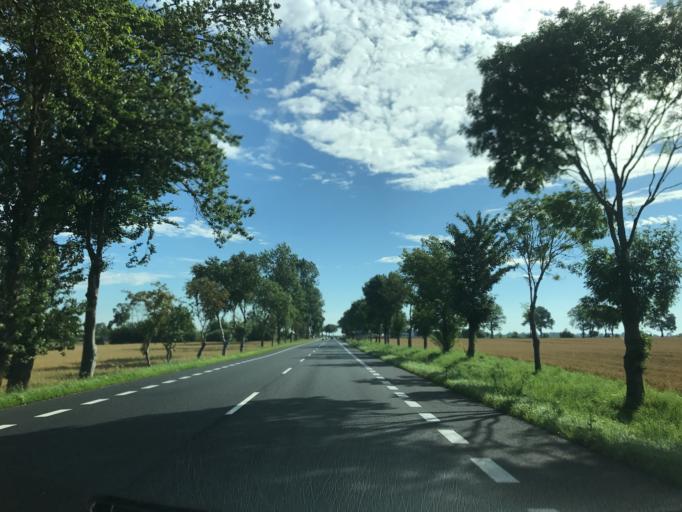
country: PL
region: West Pomeranian Voivodeship
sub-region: Powiat slawienski
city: Slawno
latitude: 54.3362
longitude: 16.5959
